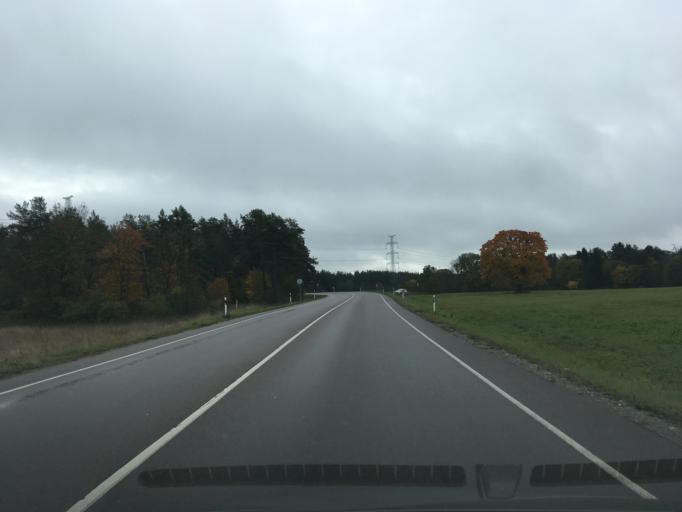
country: EE
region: Harju
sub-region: Saue vald
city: Laagri
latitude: 59.3118
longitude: 24.6127
